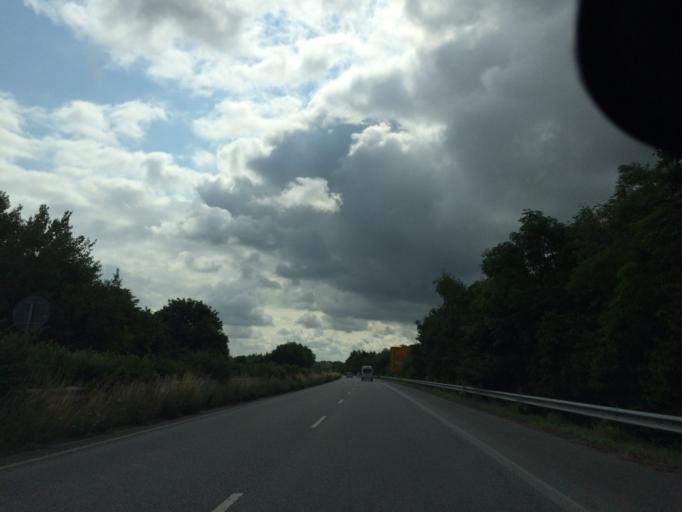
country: DE
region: Schleswig-Holstein
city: Ottendorf
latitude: 54.3788
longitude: 10.0438
